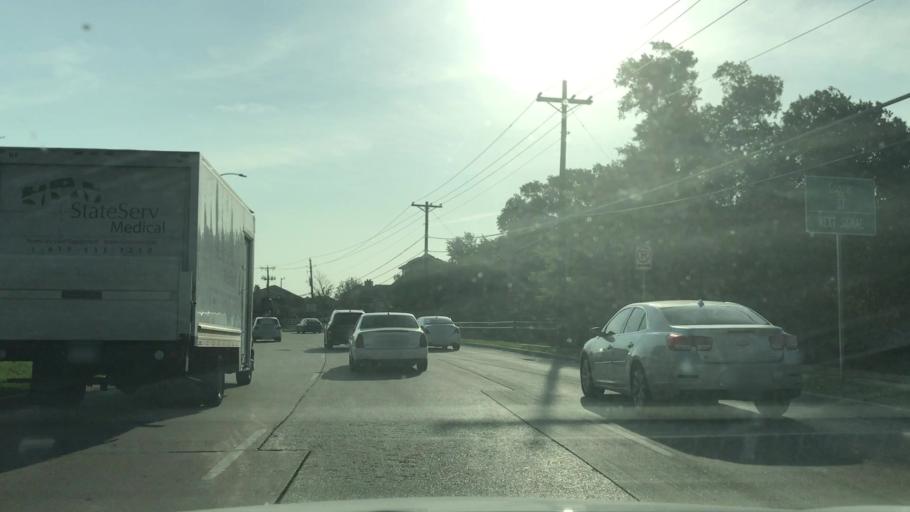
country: US
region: Texas
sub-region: Tarrant County
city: Arlington
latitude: 32.7823
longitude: -97.1163
